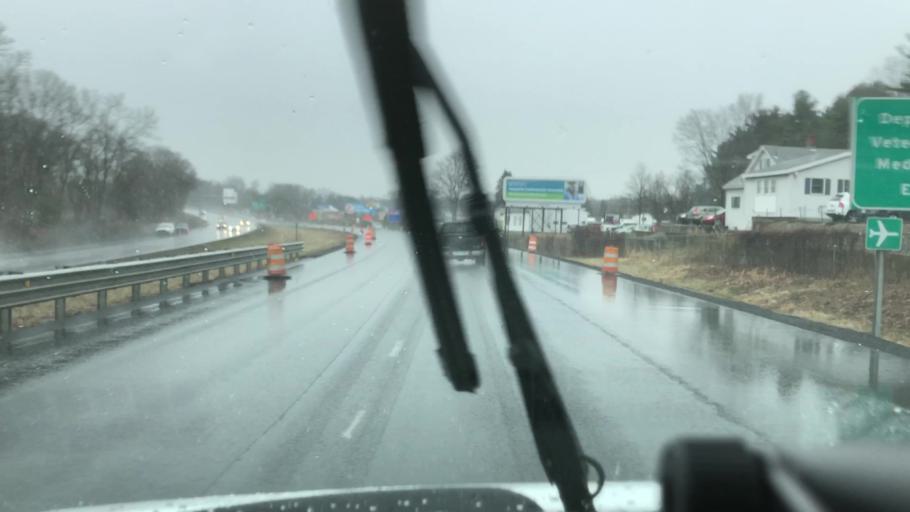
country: US
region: Massachusetts
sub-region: Hampshire County
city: Northampton
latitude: 42.3468
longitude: -72.6427
